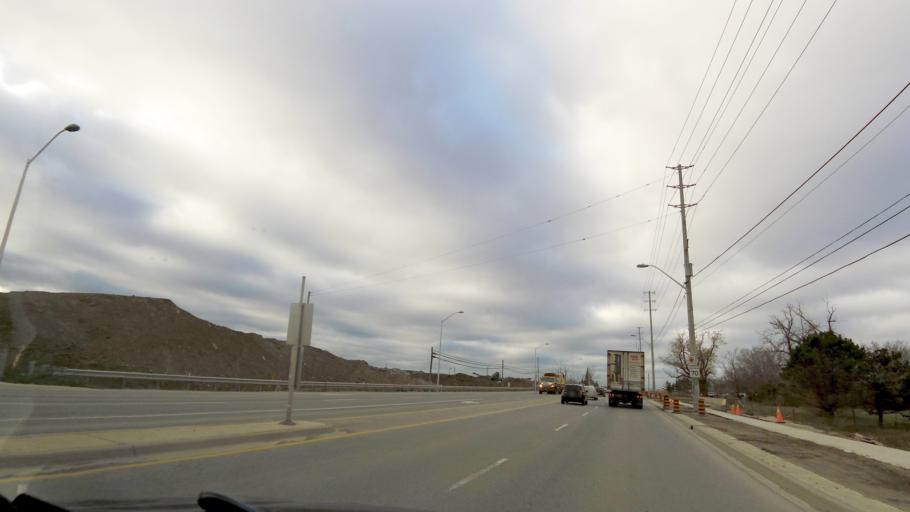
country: CA
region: Ontario
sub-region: Halton
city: Milton
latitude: 43.4870
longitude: -79.8350
